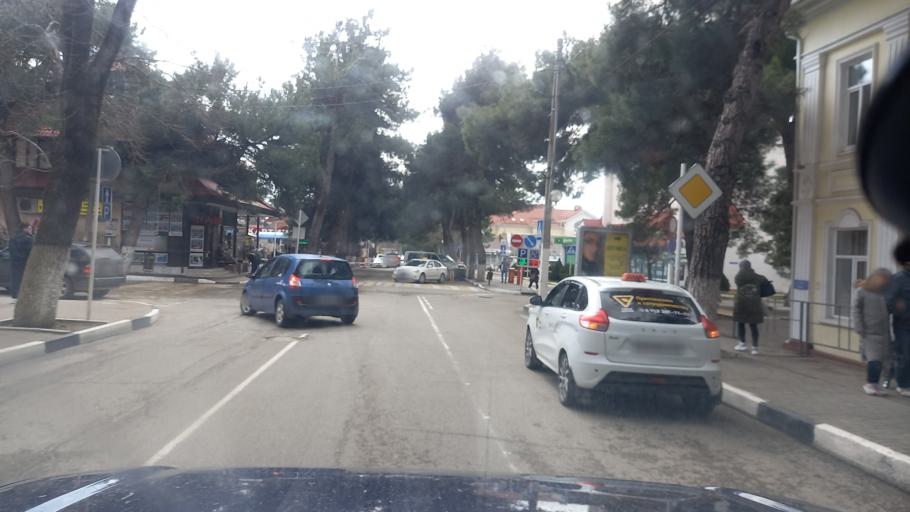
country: RU
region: Krasnodarskiy
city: Gelendzhik
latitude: 44.5628
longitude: 38.0811
